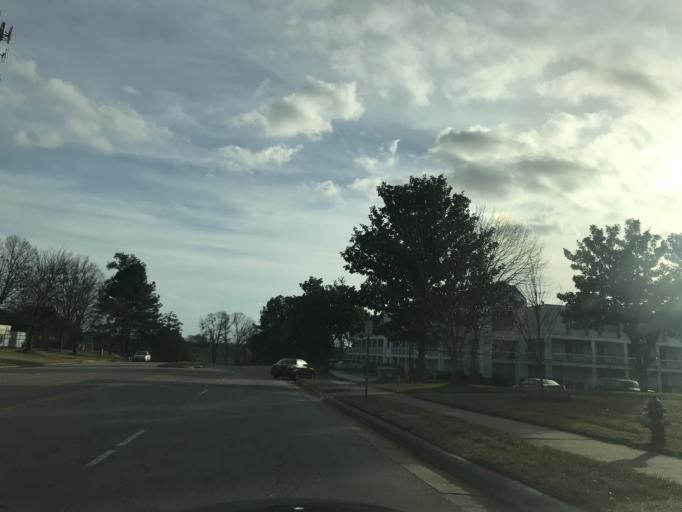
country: US
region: North Carolina
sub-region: Wake County
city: Raleigh
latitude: 35.8147
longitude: -78.6023
